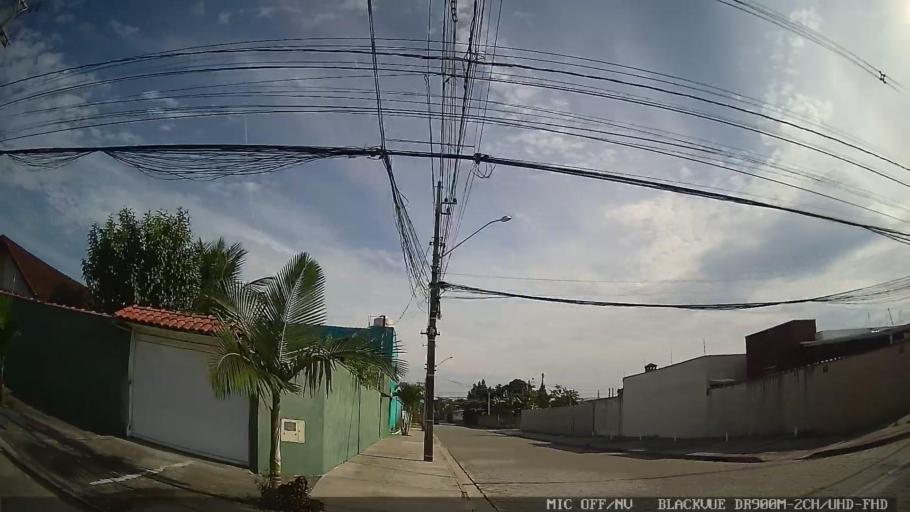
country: BR
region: Sao Paulo
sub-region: Itanhaem
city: Itanhaem
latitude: -24.1553
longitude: -46.7746
